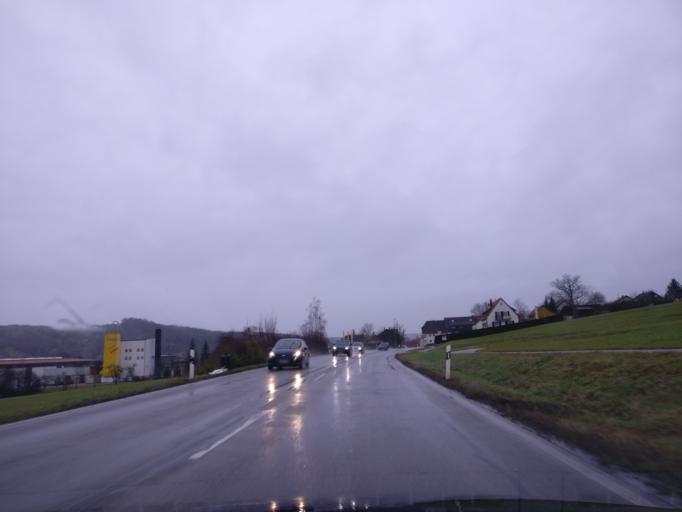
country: DE
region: Baden-Wuerttemberg
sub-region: Regierungsbezirk Stuttgart
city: Schorndorf
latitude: 48.8385
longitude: 9.5437
